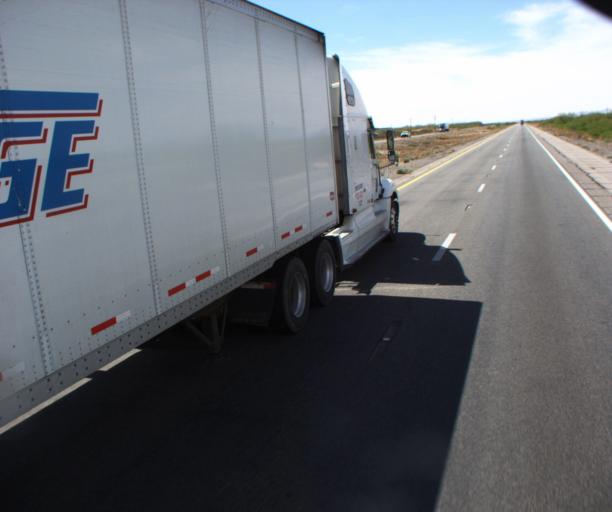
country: US
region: Arizona
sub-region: Cochise County
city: Willcox
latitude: 32.2910
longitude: -109.3255
